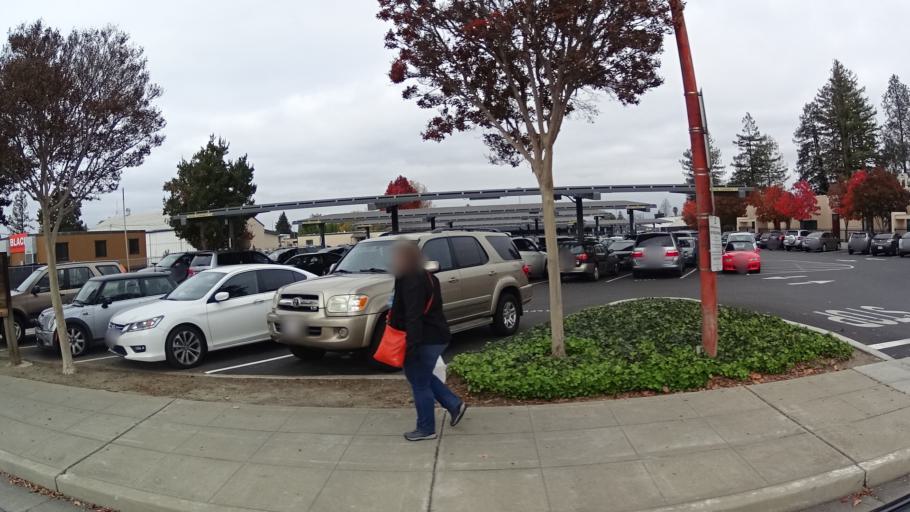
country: US
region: California
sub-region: Santa Clara County
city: Sunnyvale
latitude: 37.3522
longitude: -122.0361
